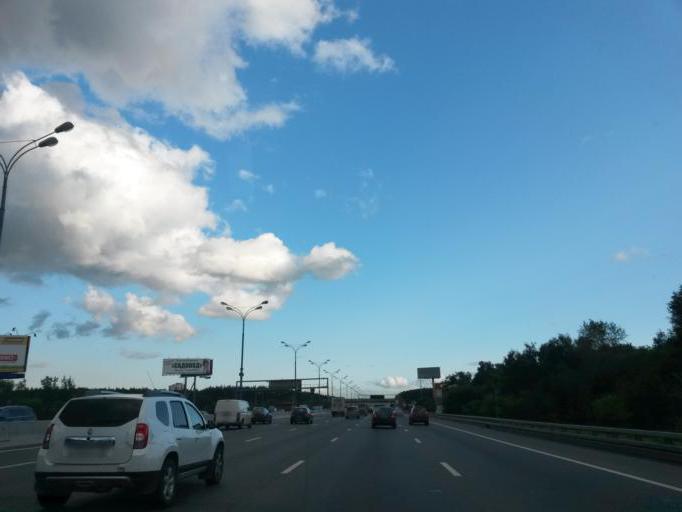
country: RU
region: Moscow
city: Zhulebino
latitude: 55.6727
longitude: 37.8358
